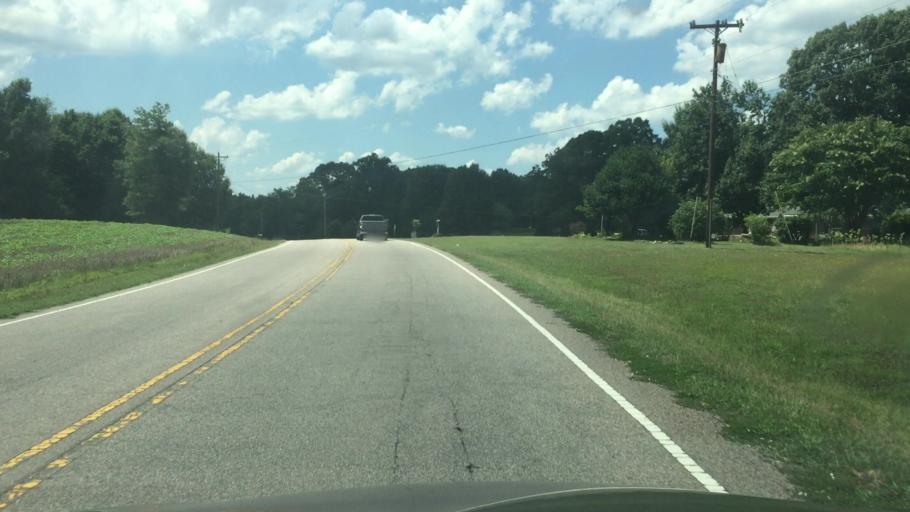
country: US
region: North Carolina
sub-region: Rowan County
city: Enochville
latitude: 35.5762
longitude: -80.6905
